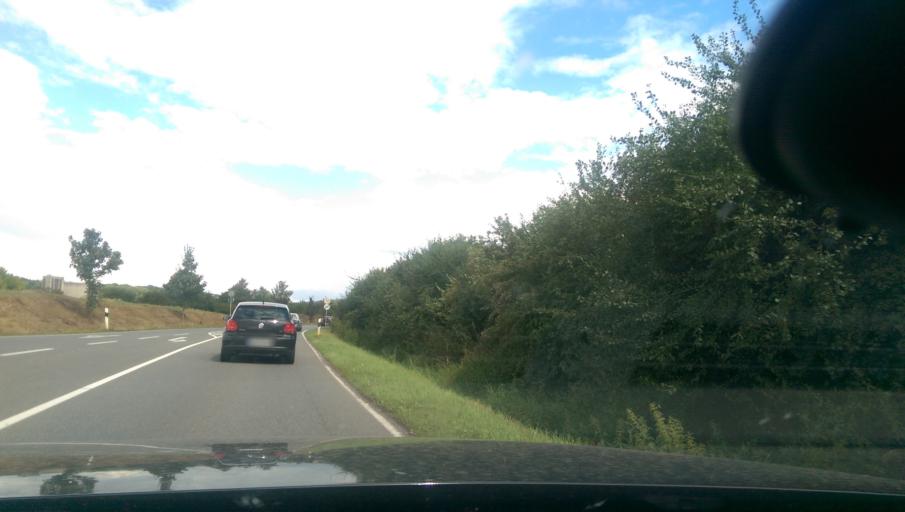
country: DE
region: Lower Saxony
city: Northeim
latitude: 51.7113
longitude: 9.9801
